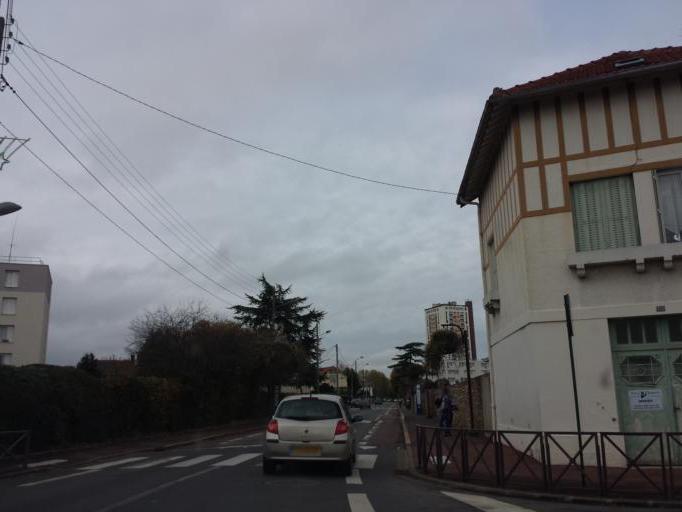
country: FR
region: Ile-de-France
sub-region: Departement du Val-d'Oise
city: Ermont
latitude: 48.9938
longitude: 2.2572
